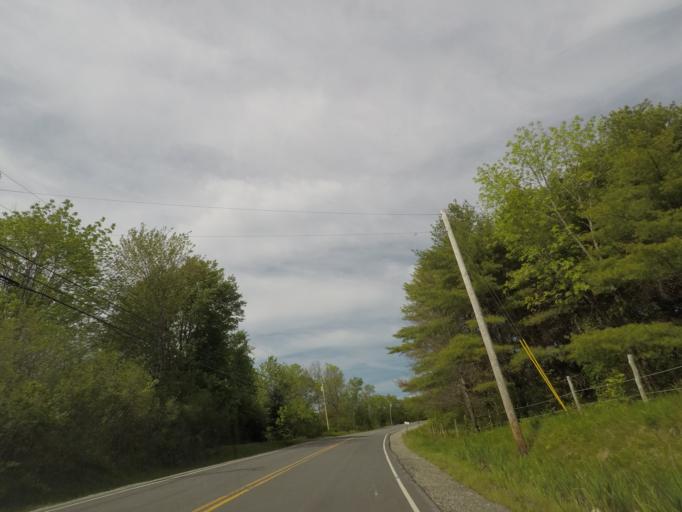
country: US
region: Maine
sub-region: Sagadahoc County
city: Richmond
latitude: 44.0937
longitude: -69.7430
